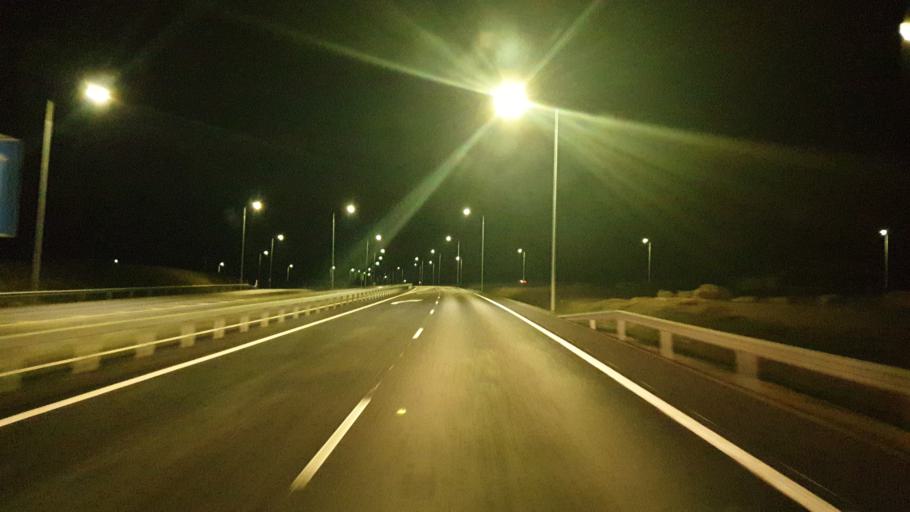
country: FI
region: Central Finland
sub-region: AEaenekoski
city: AEaenekoski
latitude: 62.6090
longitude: 25.6892
